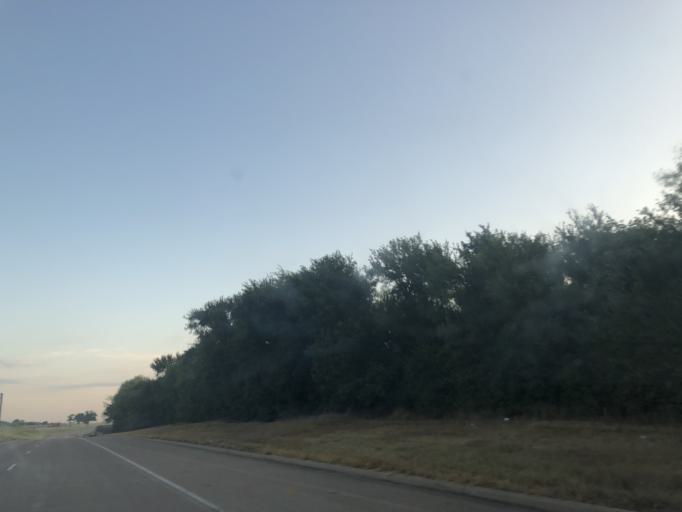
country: US
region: Texas
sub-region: Tarrant County
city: Euless
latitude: 32.8456
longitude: -97.0616
